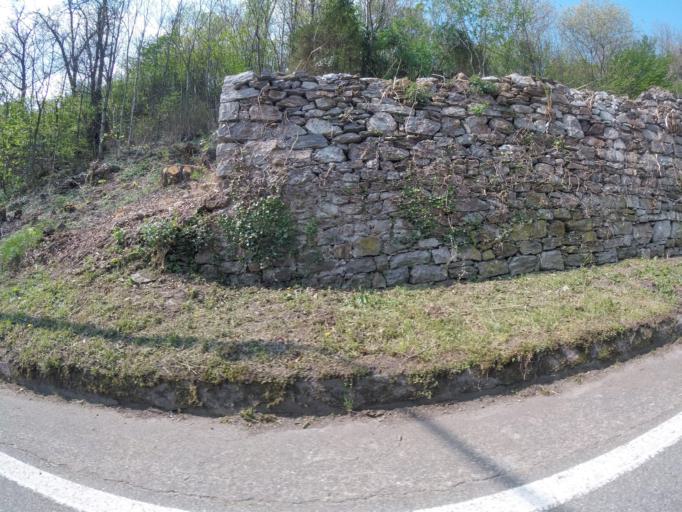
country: IT
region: Piedmont
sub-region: Provincia di Novara
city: Orta San Giulio
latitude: 45.8011
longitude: 8.4106
